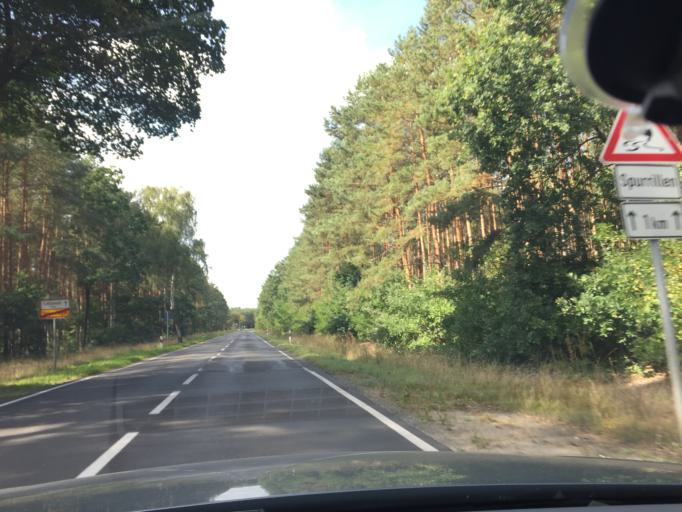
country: DE
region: Brandenburg
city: Spreenhagen
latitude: 52.3503
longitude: 13.8682
